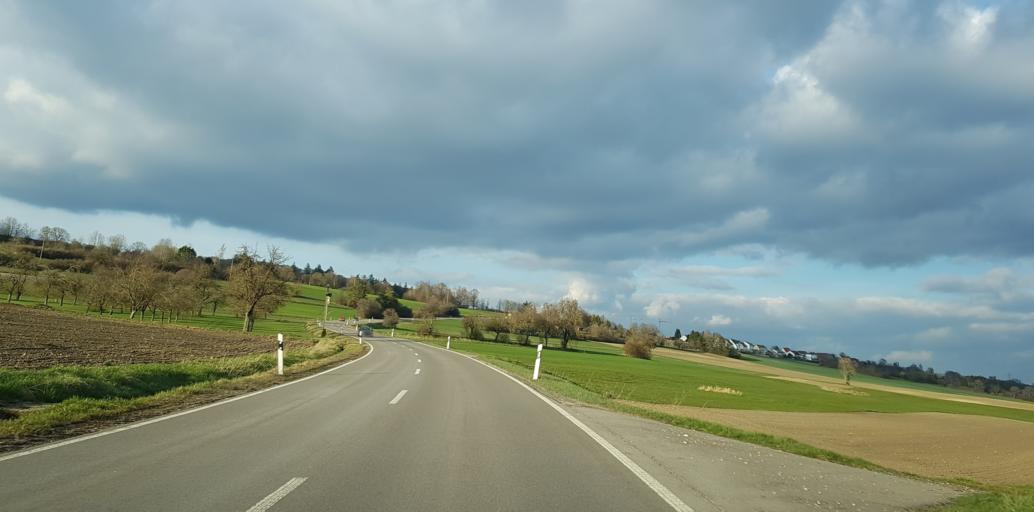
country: DE
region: Baden-Wuerttemberg
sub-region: Tuebingen Region
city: Erbach
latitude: 48.3709
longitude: 9.8815
